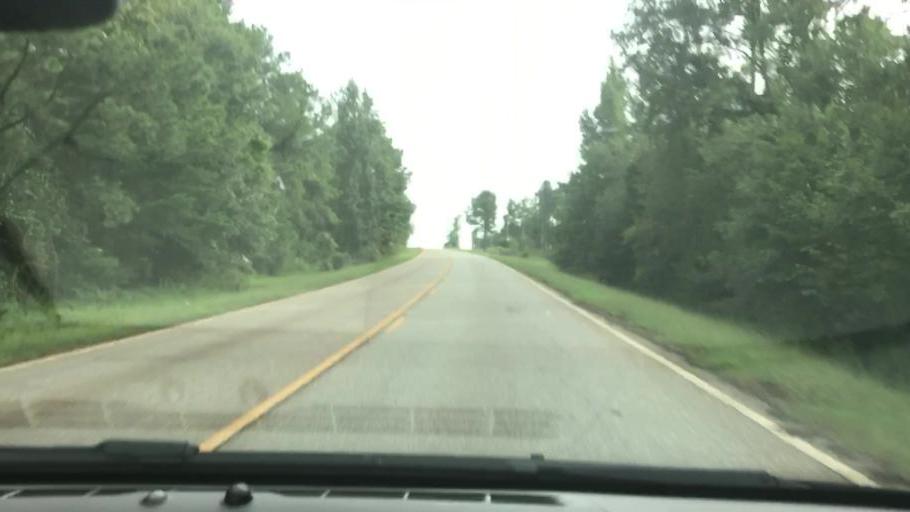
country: US
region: Georgia
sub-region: Quitman County
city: Georgetown
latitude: 31.9266
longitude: -85.0176
